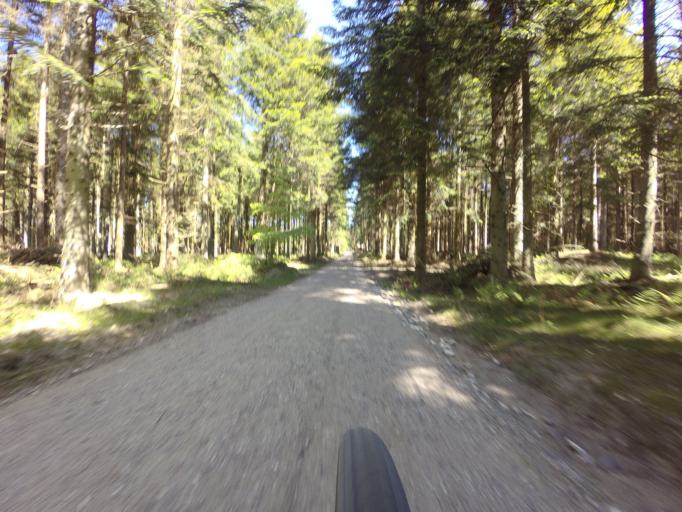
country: DK
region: North Denmark
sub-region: Jammerbugt Kommune
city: Pandrup
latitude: 57.2421
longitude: 9.6034
